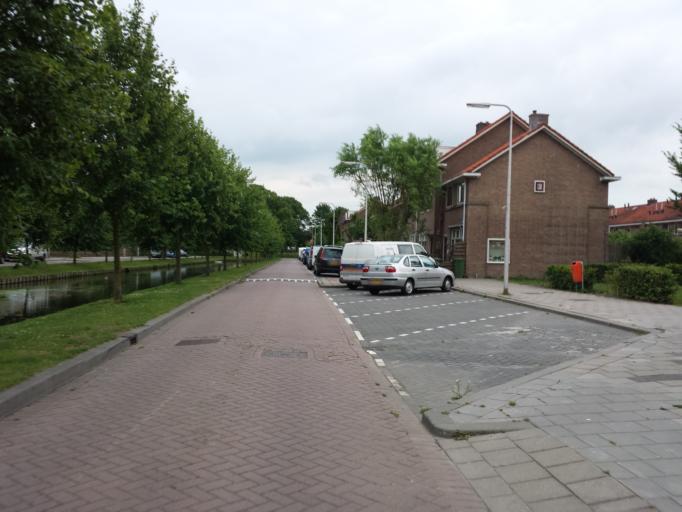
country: NL
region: South Holland
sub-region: Gemeente Gouda
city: Gouda
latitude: 52.0021
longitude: 4.7007
